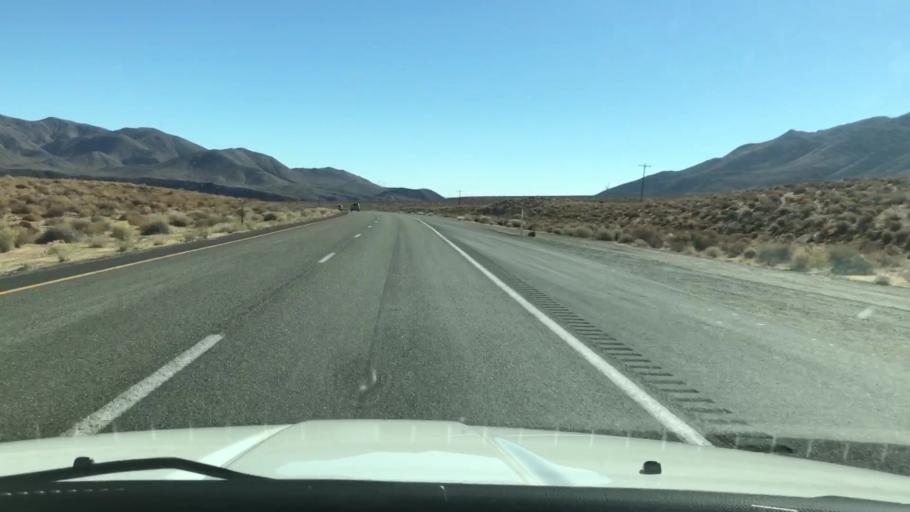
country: US
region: California
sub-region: Kern County
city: Inyokern
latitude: 35.9673
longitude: -117.9206
